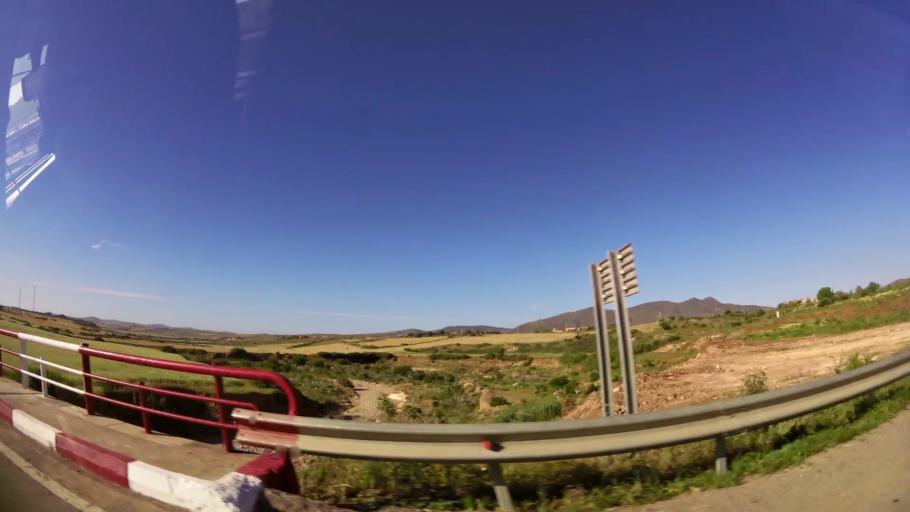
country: MA
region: Oriental
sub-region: Berkane-Taourirt
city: Ahfir
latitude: 34.9819
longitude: -2.1409
